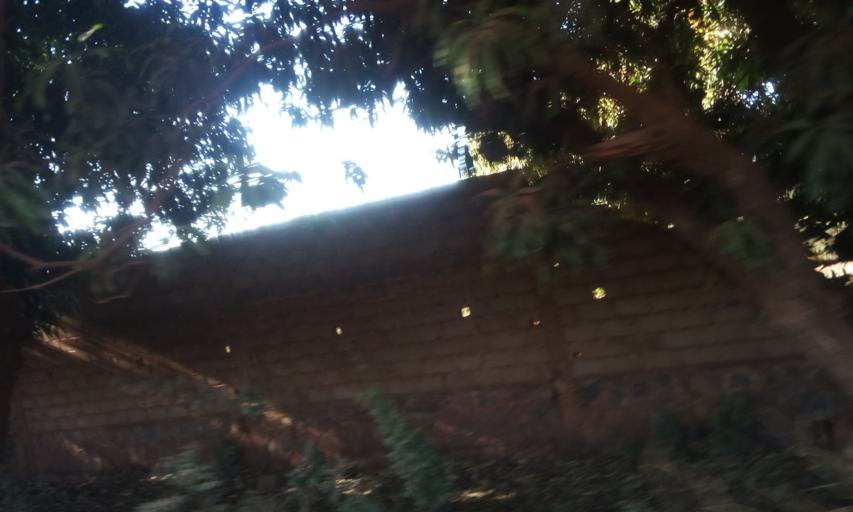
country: ML
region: Bamako
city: Bamako
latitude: 12.6410
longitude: -7.9092
